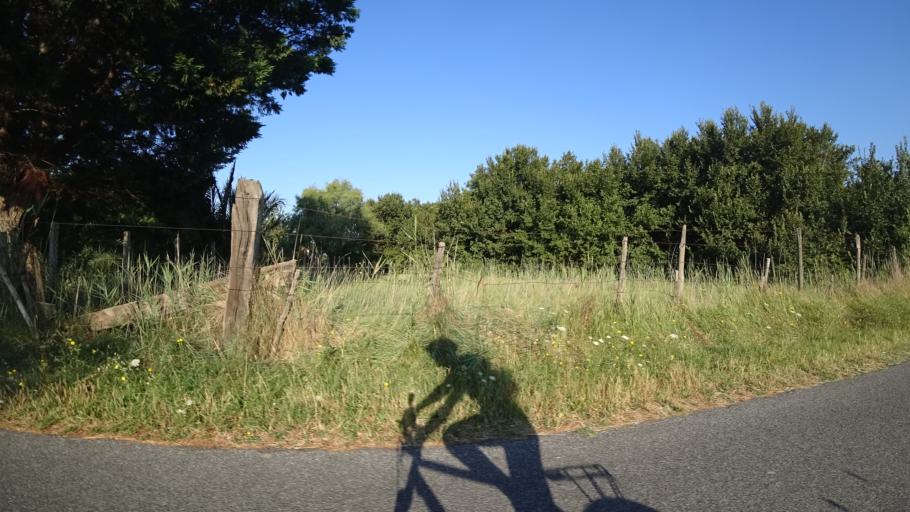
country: FR
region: Languedoc-Roussillon
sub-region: Departement des Pyrenees-Orientales
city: Sainte-Marie-Plage
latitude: 42.7266
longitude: 3.0291
